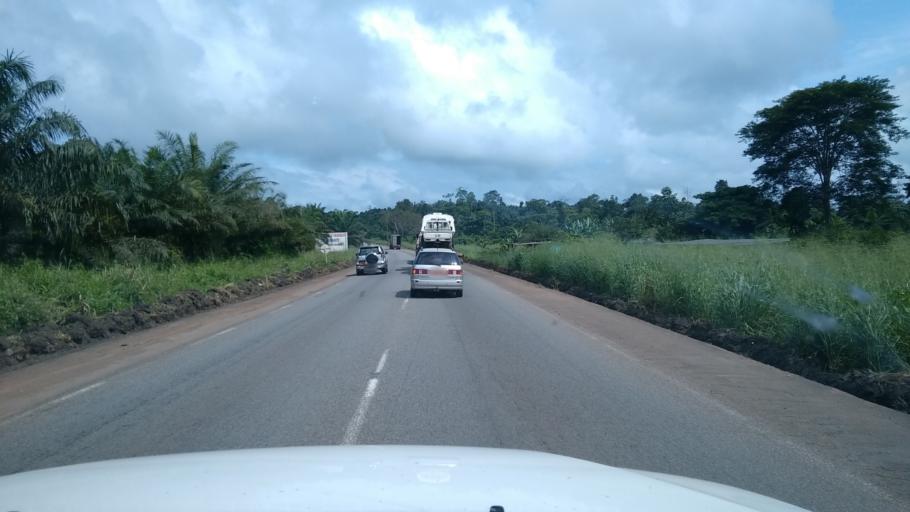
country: CM
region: Littoral
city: Edea
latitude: 3.9256
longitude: 10.0586
